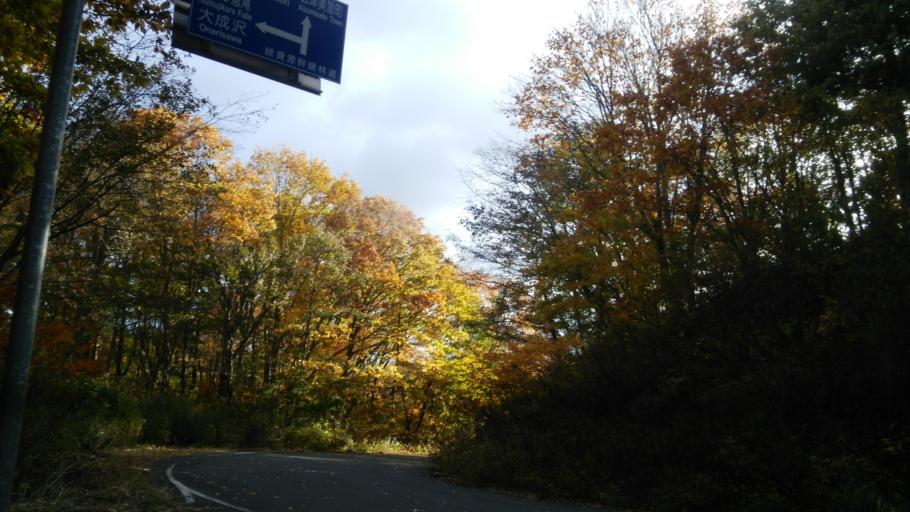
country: JP
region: Fukushima
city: Kitakata
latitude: 37.3845
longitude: 139.7322
